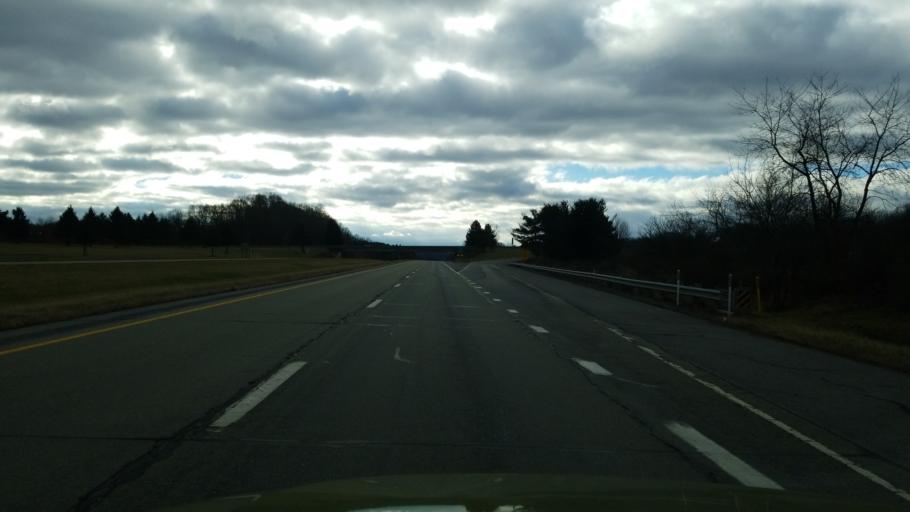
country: US
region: Pennsylvania
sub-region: Indiana County
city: Chevy Chase Heights
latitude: 40.6301
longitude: -79.1176
